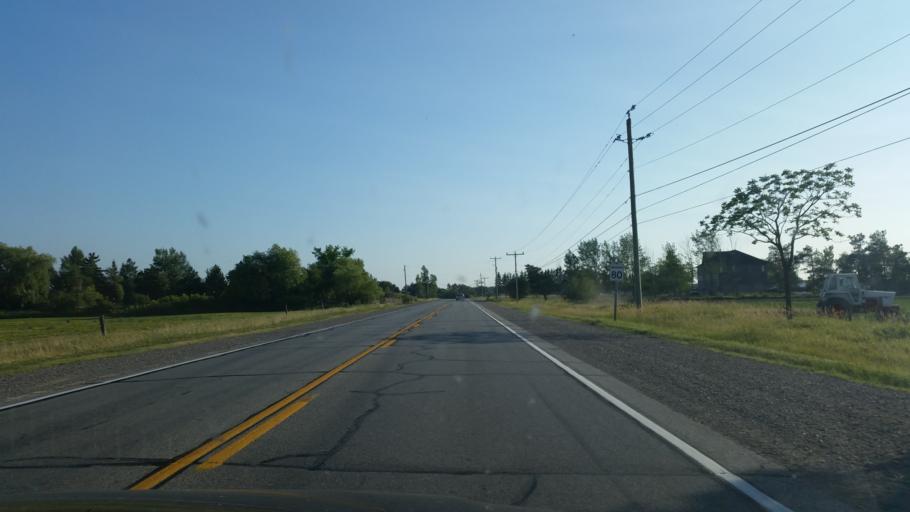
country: CA
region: Ontario
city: Brampton
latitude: 43.8218
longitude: -79.8259
